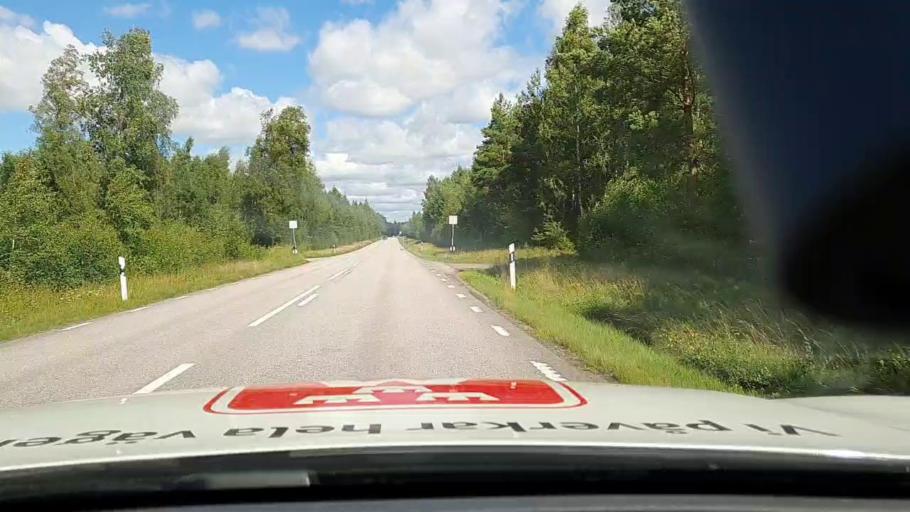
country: SE
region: Vaestra Goetaland
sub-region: Skovde Kommun
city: Stopen
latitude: 58.4460
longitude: 13.9409
